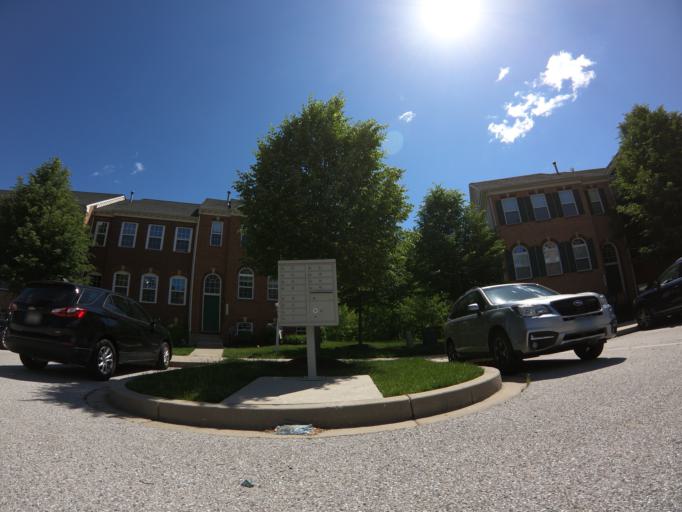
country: US
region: Maryland
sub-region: Howard County
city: Columbia
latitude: 39.3112
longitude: -76.8897
